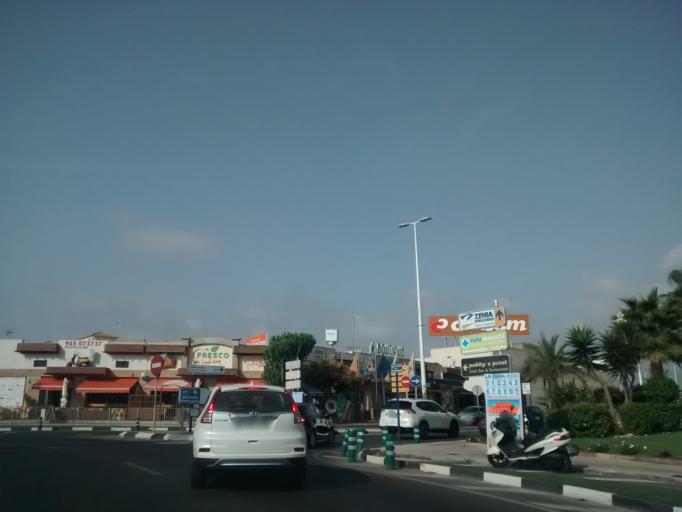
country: ES
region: Valencia
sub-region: Provincia de Alicante
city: Torrevieja
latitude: 37.9257
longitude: -0.7290
